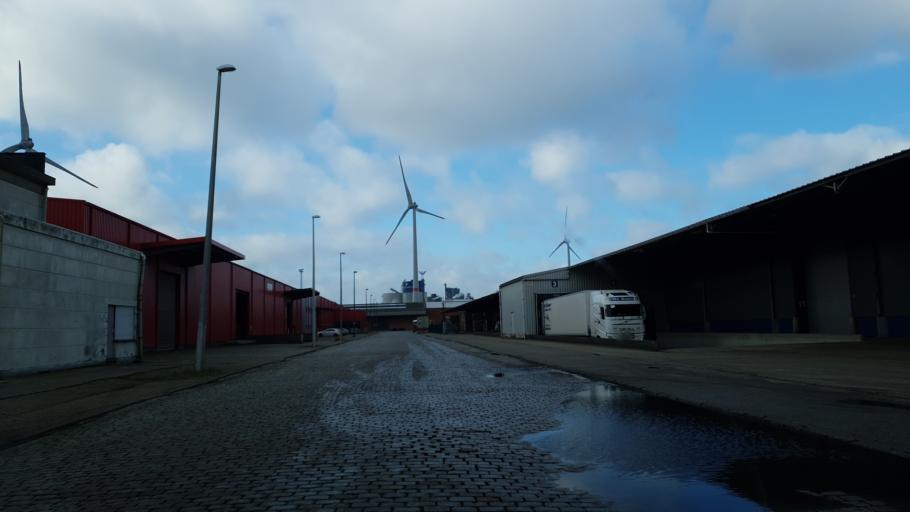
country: BE
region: Flanders
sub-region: Provincie Antwerpen
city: Stabroek
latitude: 51.2741
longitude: 4.3725
